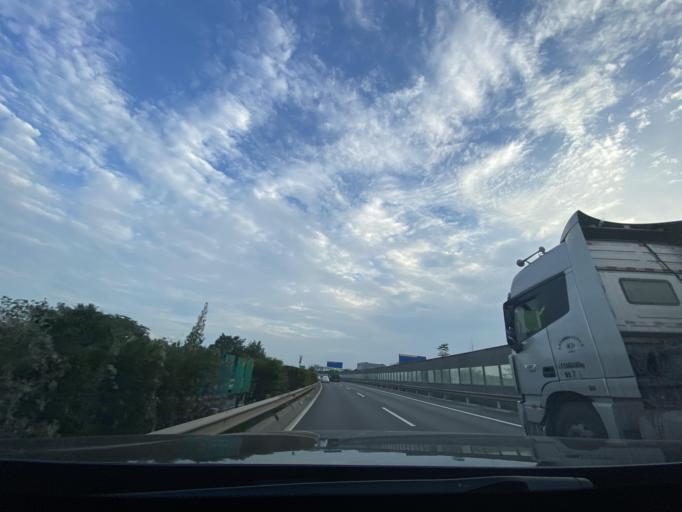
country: CN
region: Sichuan
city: Deyang
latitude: 31.0783
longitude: 104.3819
